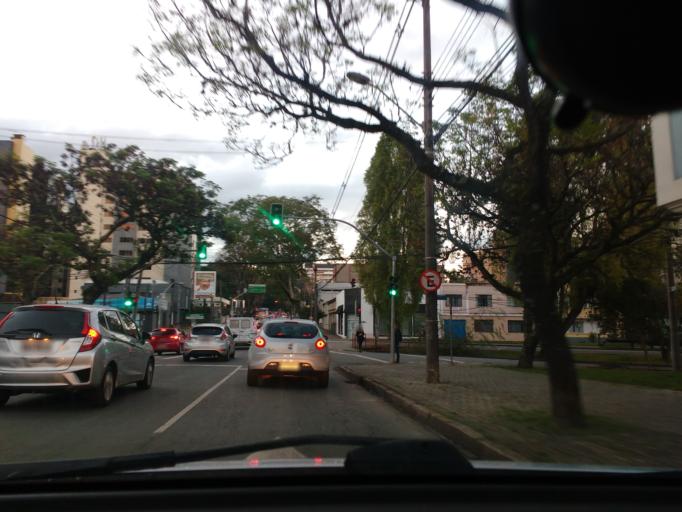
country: BR
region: Parana
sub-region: Curitiba
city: Curitiba
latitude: -25.4300
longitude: -49.2839
